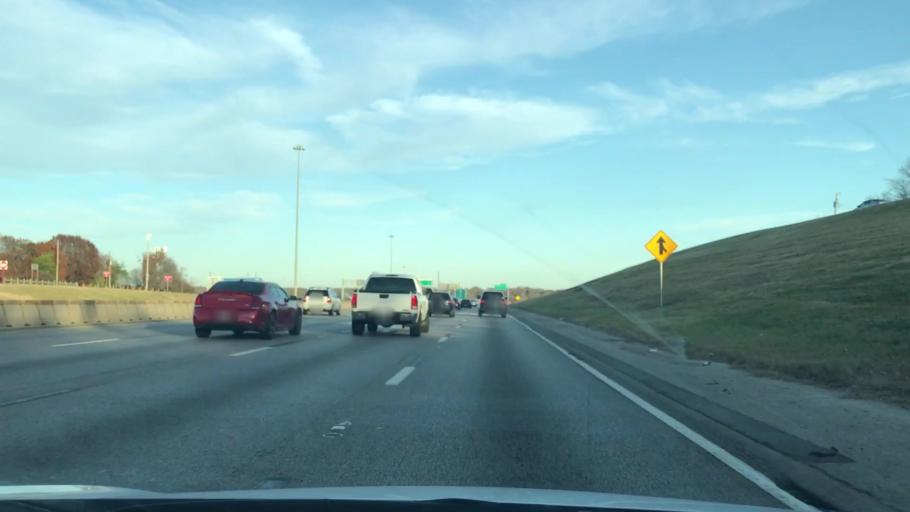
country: US
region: Texas
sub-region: Dallas County
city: Highland Park
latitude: 32.7914
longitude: -96.7367
